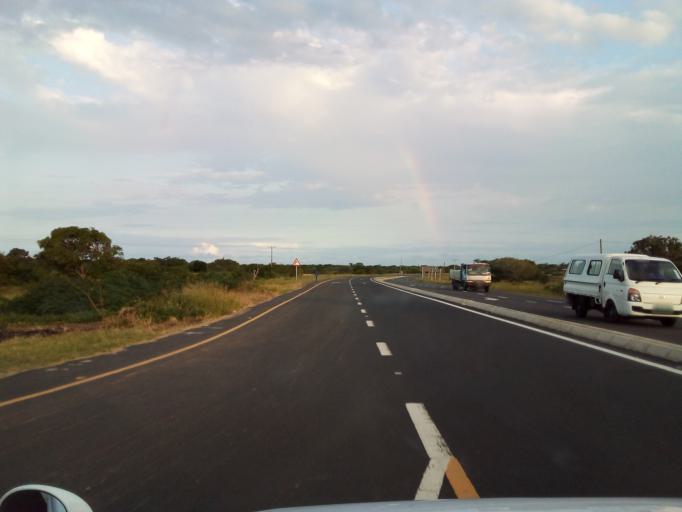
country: MZ
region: Maputo City
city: Maputo
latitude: -26.0797
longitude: 32.6203
